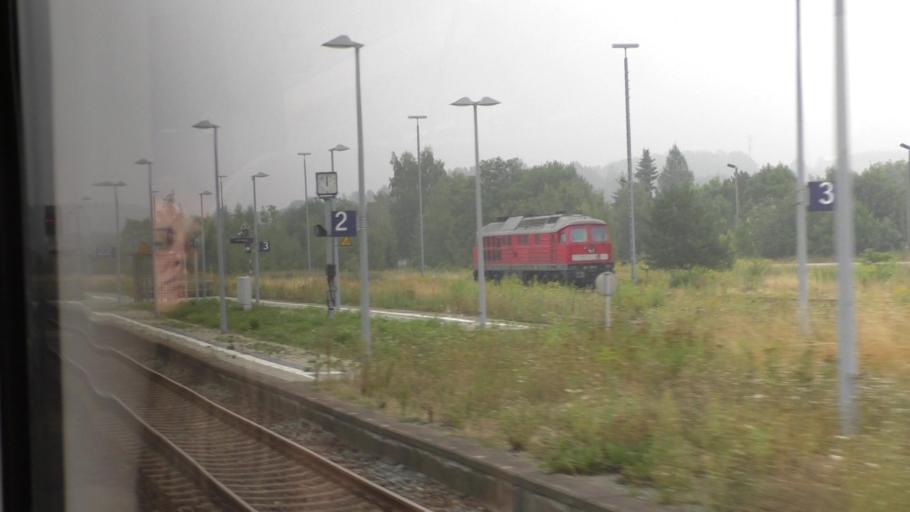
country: DE
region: Saxony
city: Ebersbach
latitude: 51.0039
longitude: 14.5787
